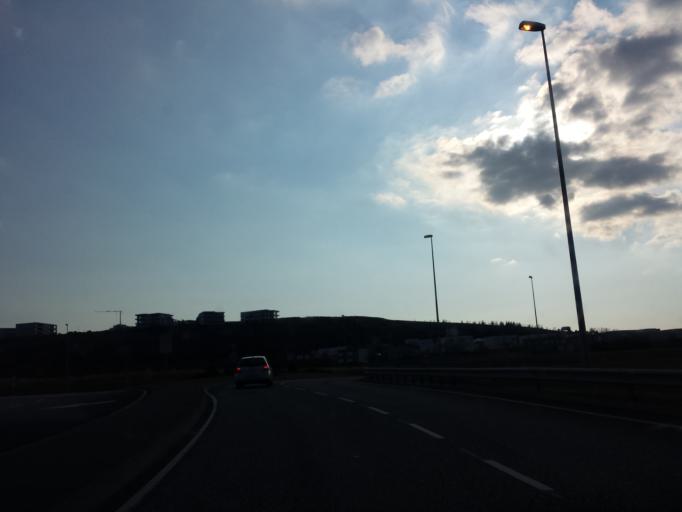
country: IS
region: Capital Region
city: Reykjavik
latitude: 64.0907
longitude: -21.8581
